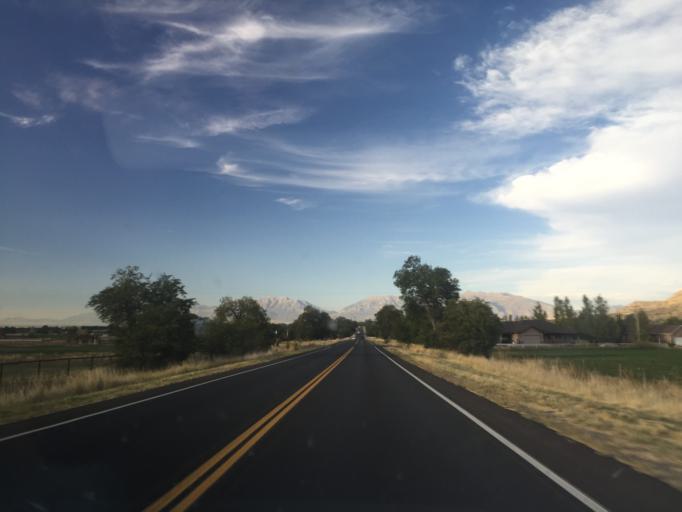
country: US
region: Utah
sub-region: Utah County
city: Santaquin
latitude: 39.9965
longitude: -111.7528
